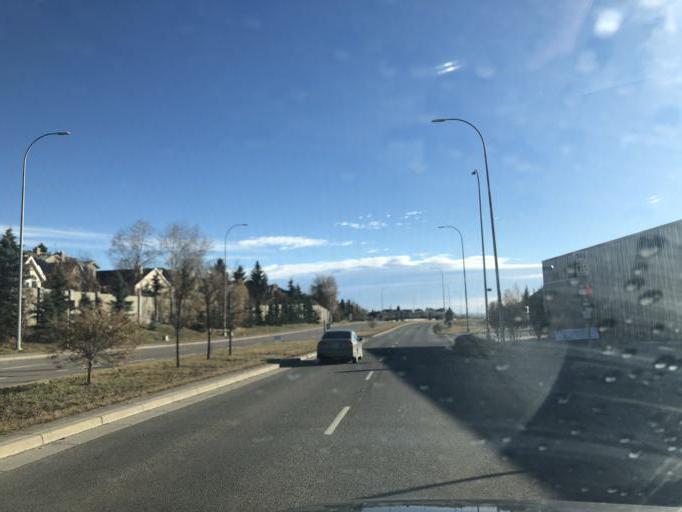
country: CA
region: Alberta
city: Calgary
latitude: 51.0378
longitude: -114.1862
